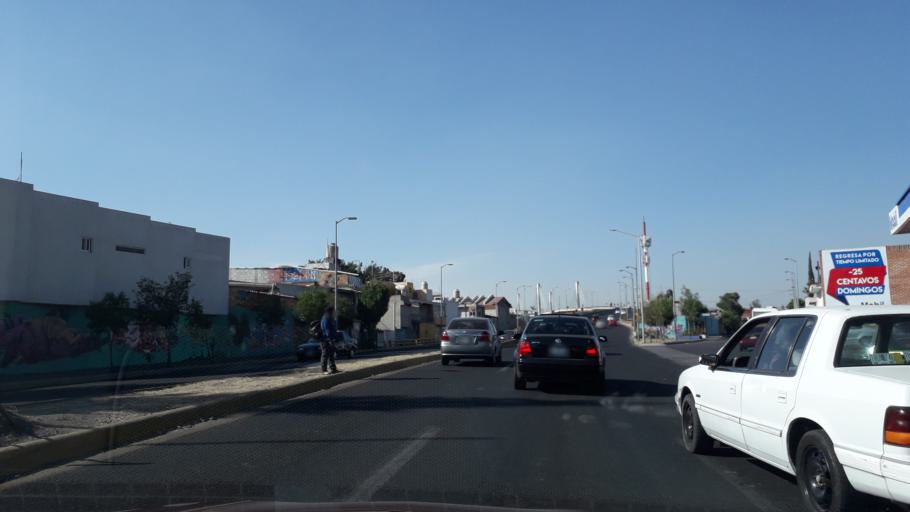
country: MX
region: Puebla
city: Puebla
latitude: 19.0750
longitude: -98.1904
